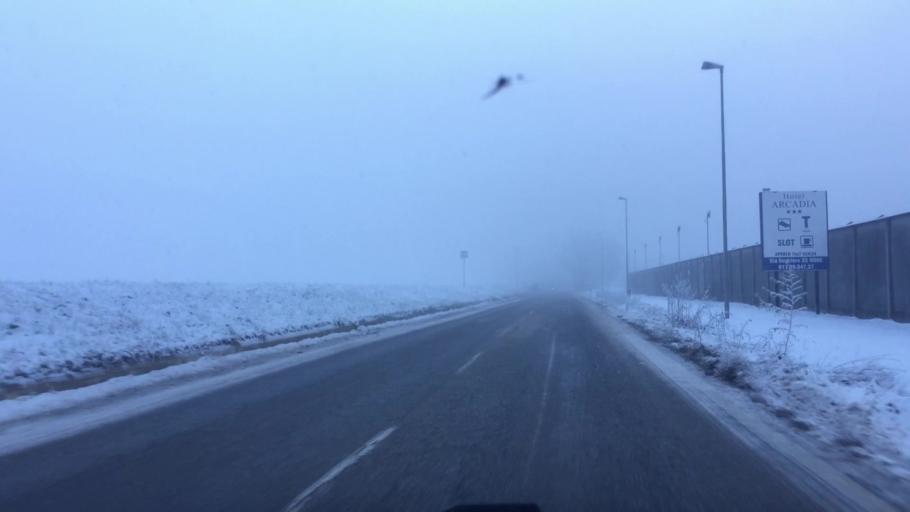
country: IT
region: Piedmont
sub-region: Provincia di Torino
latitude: 44.9393
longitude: 7.5313
